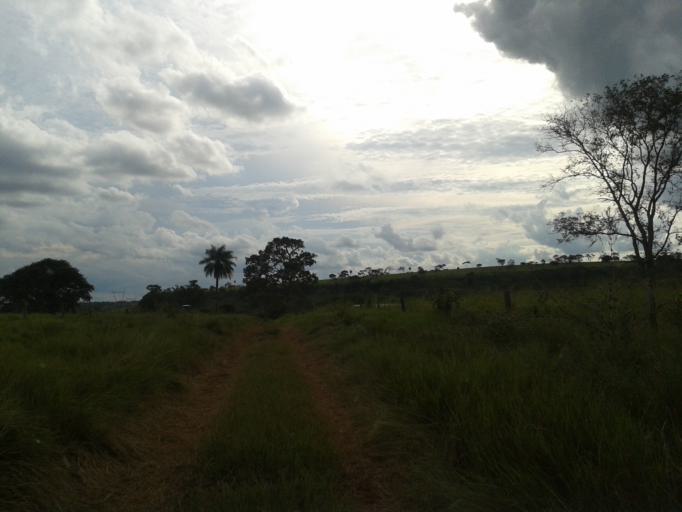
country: BR
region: Minas Gerais
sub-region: Campina Verde
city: Campina Verde
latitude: -19.4397
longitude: -49.5954
